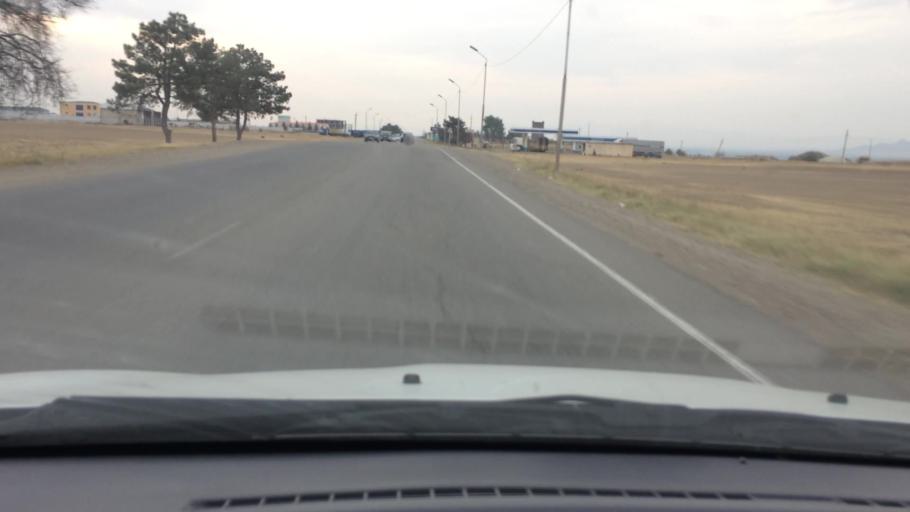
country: GE
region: Kvemo Kartli
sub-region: Marneuli
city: Marneuli
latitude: 41.5118
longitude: 44.7906
